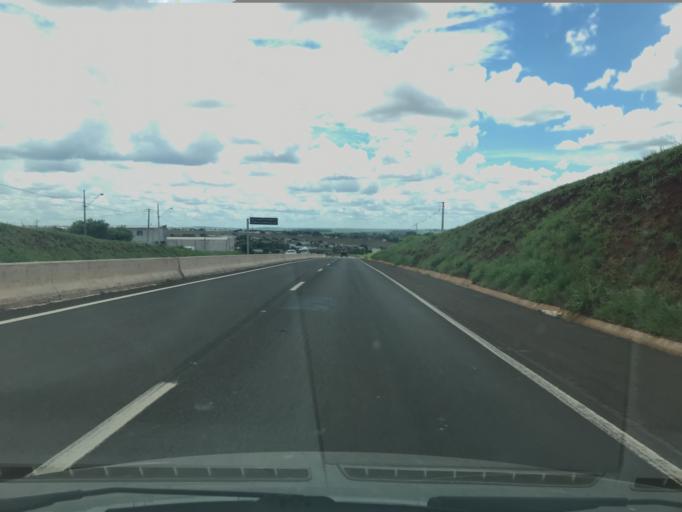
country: BR
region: Parana
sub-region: Maringa
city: Maringa
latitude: -23.3744
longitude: -51.9200
